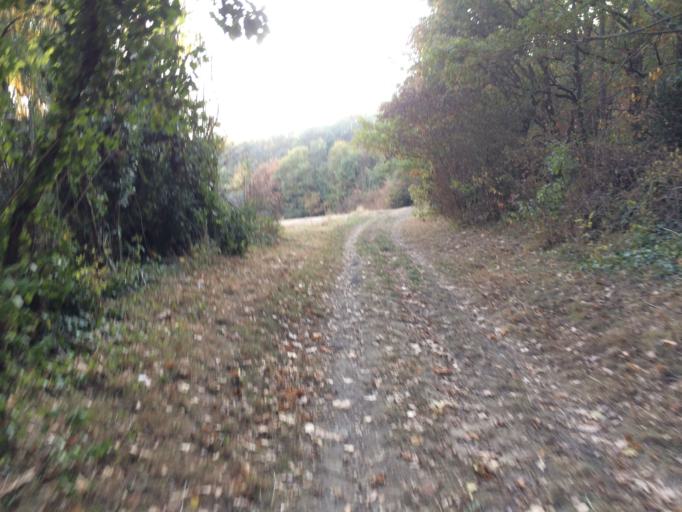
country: FR
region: Ile-de-France
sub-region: Departement de l'Essonne
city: Villejust
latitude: 48.6888
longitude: 2.2432
